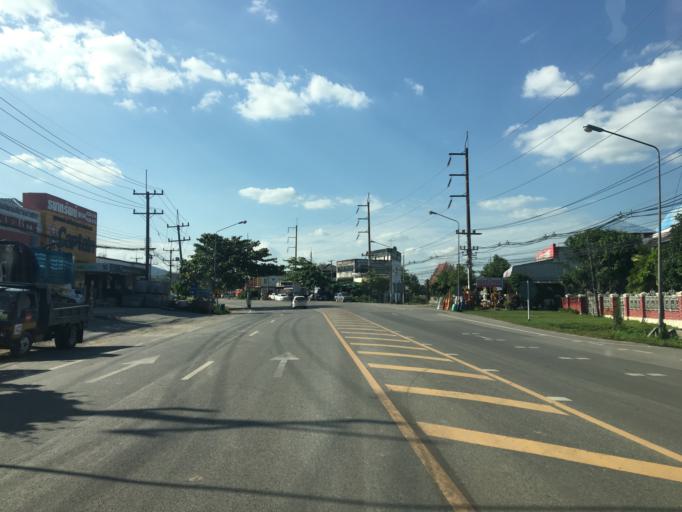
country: TH
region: Phayao
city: Chun
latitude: 19.3384
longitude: 100.1305
